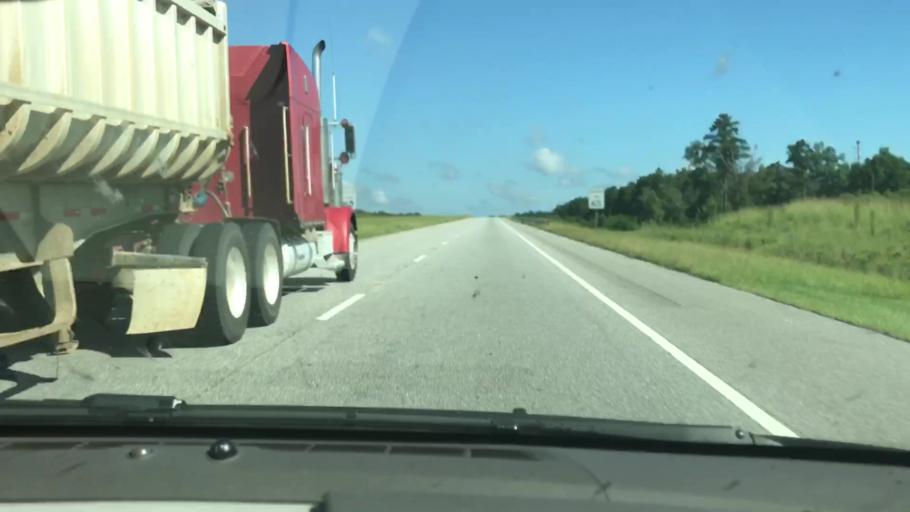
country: US
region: Alabama
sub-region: Barbour County
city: Eufaula
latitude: 32.1180
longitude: -85.1511
